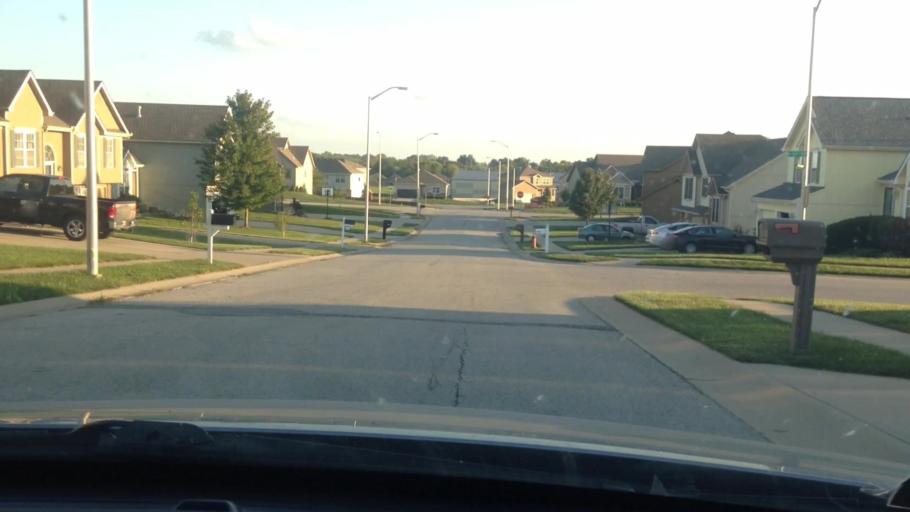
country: US
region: Missouri
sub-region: Clay County
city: Smithville
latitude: 39.2989
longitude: -94.5872
